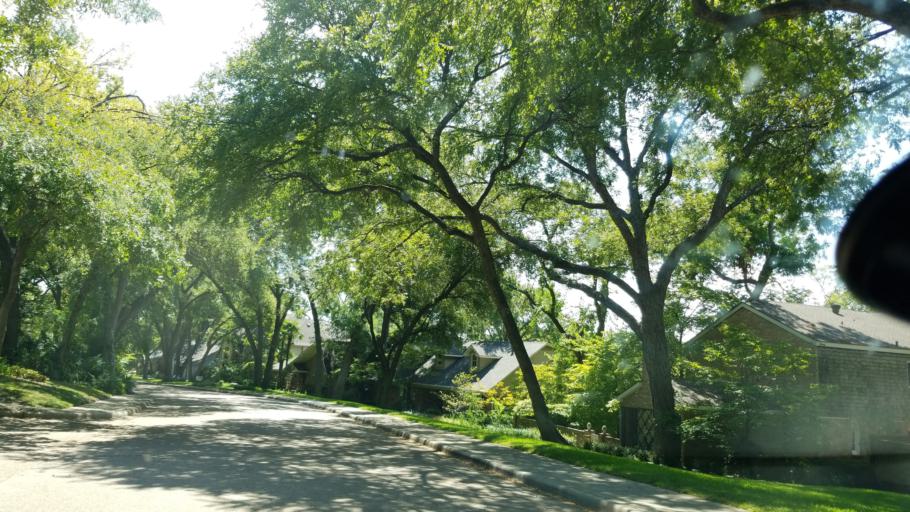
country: US
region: Texas
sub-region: Dallas County
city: Richardson
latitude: 32.8823
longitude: -96.7117
